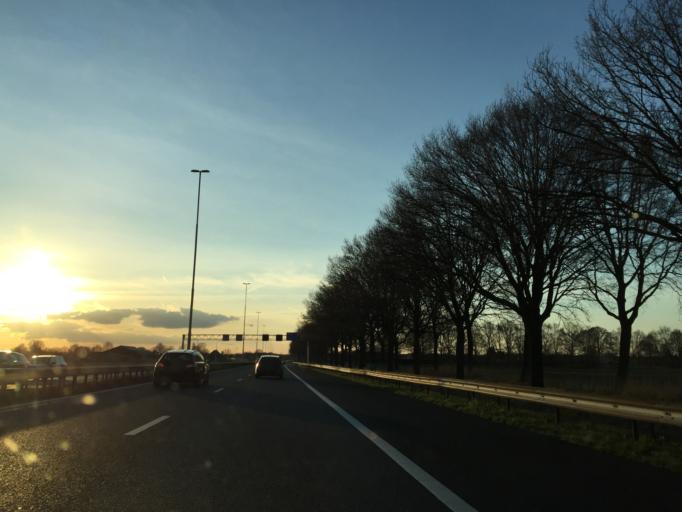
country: NL
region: North Brabant
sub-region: Gemeente Oisterwijk
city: Oisterwijk
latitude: 51.5332
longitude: 5.1877
